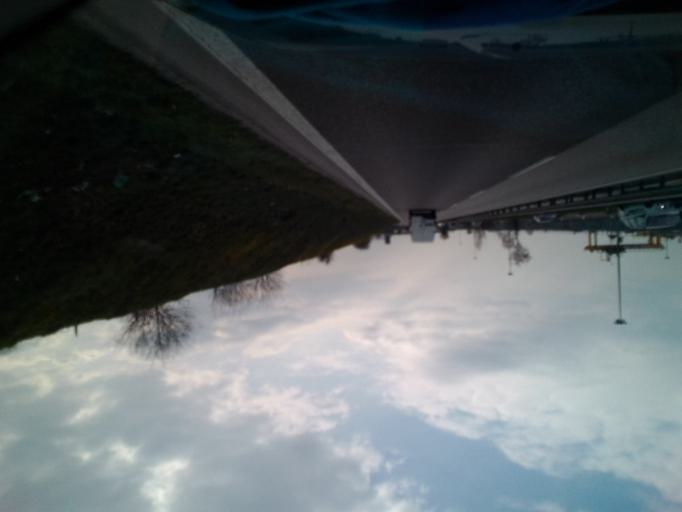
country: IT
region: Veneto
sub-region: Provincia di Verona
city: Caselle
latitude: 45.4227
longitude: 10.9147
